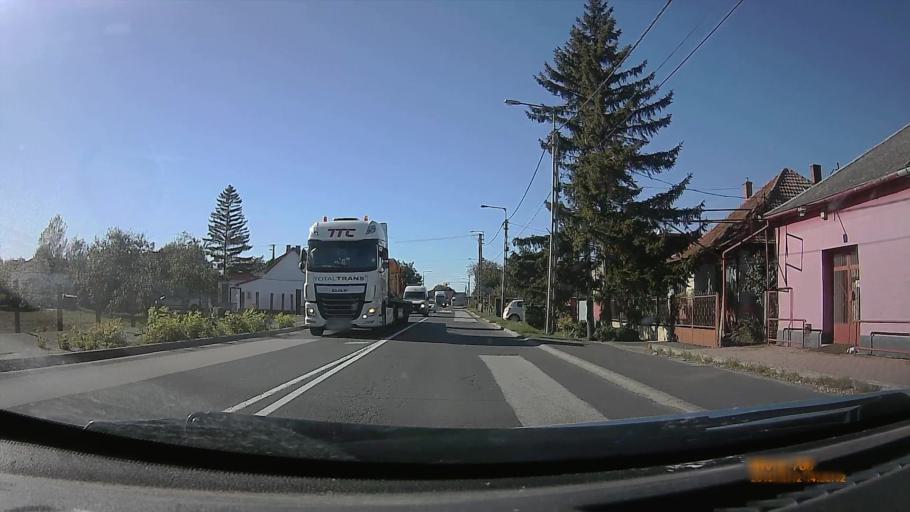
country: HU
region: Hajdu-Bihar
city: Berettyoujfalu
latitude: 47.1680
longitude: 21.6215
